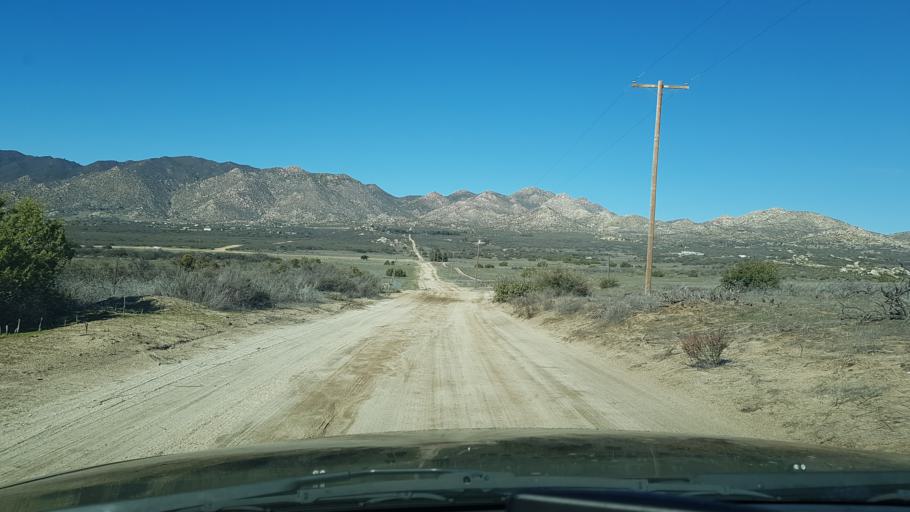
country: US
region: California
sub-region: San Diego County
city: Borrego Springs
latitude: 33.2044
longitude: -116.5082
